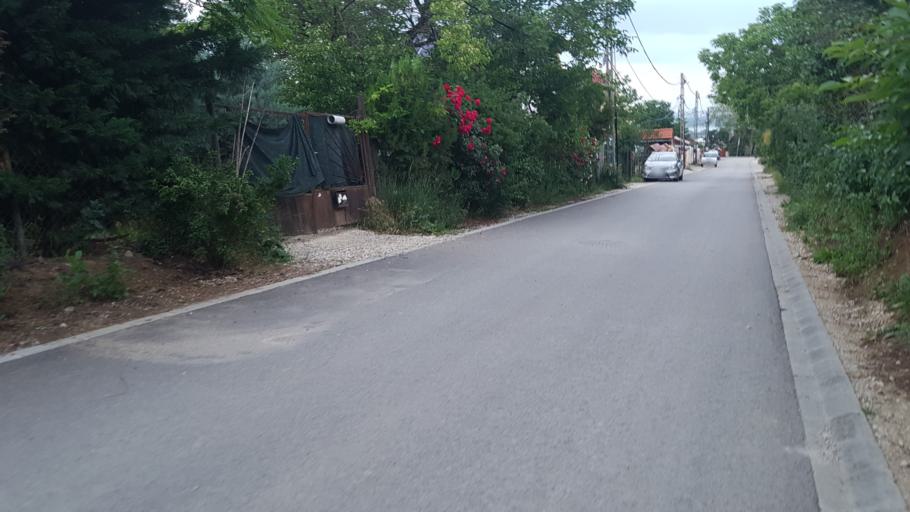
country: HU
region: Pest
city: Budakalasz
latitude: 47.6159
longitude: 19.0478
